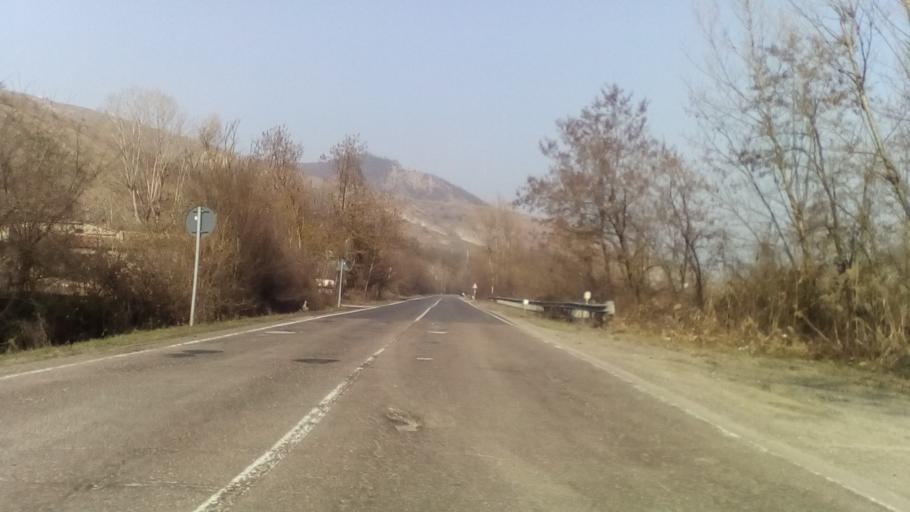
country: IT
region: Emilia-Romagna
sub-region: Provincia di Modena
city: Serramazzoni
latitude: 44.4639
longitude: 10.8378
